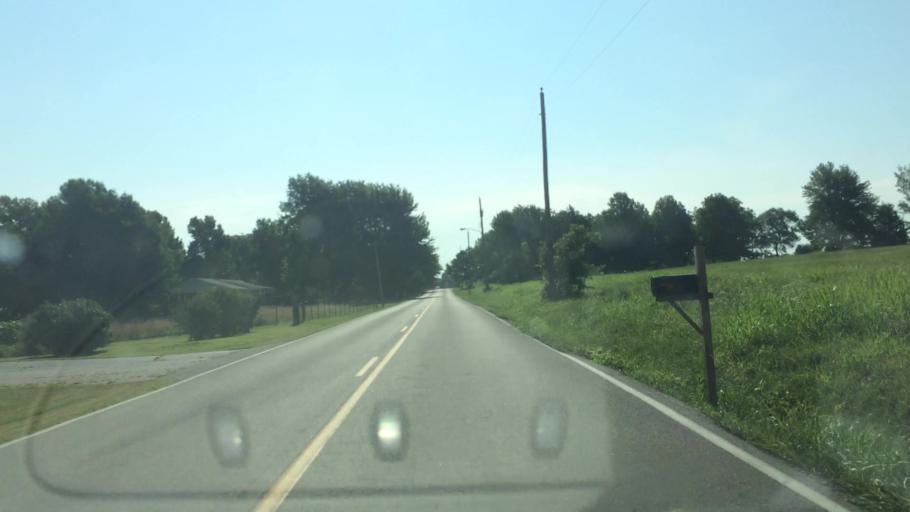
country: US
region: Missouri
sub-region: Greene County
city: Strafford
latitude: 37.2556
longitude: -93.1758
